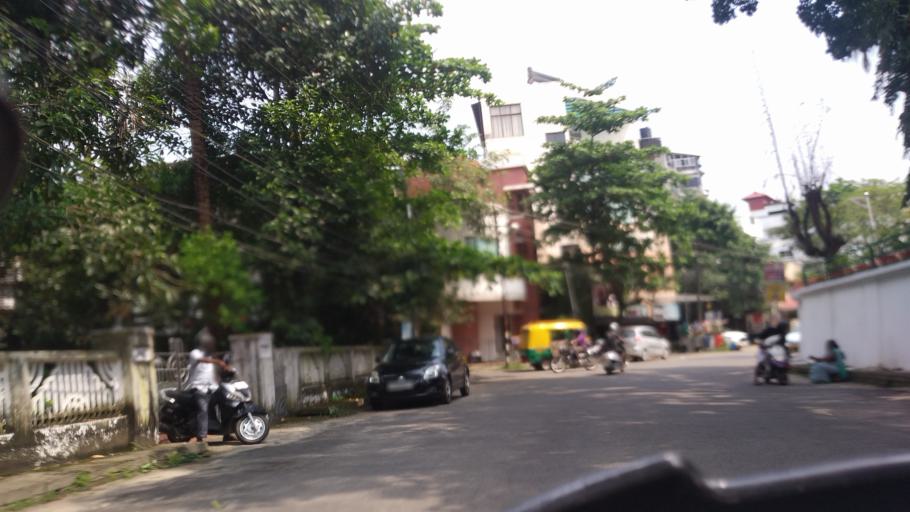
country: IN
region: Kerala
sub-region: Ernakulam
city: Cochin
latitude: 9.9700
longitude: 76.2835
